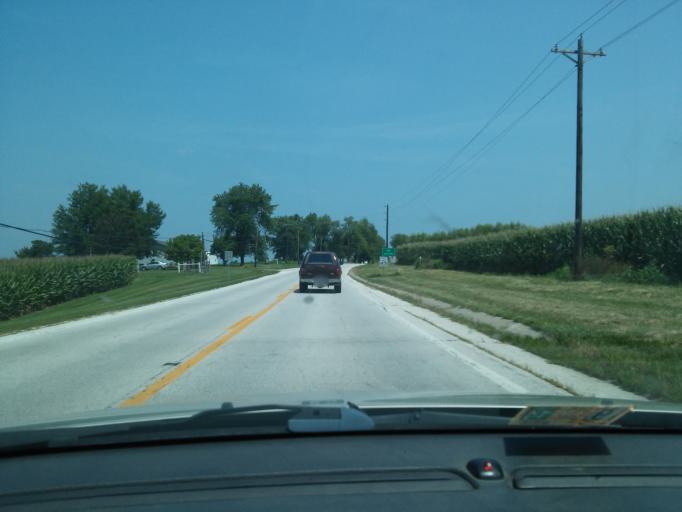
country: US
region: Illinois
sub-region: Pike County
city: Pittsfield
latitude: 39.5709
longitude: -90.9133
